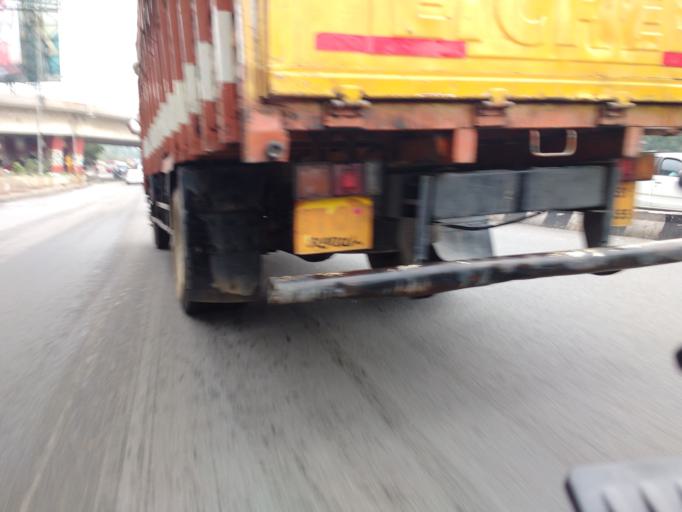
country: IN
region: Karnataka
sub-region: Bangalore Urban
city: Bangalore
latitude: 12.9950
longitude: 77.6650
